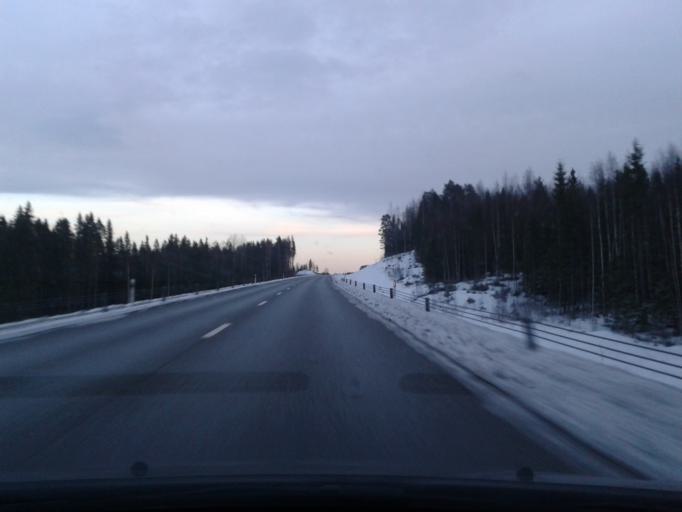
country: SE
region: Vaesternorrland
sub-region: Kramfors Kommun
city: Bollstabruk
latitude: 63.0668
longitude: 17.5826
